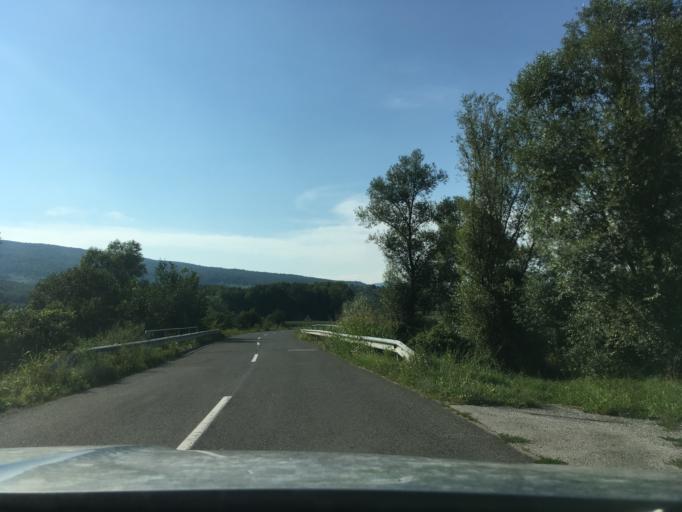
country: SI
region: Crnomelj
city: Crnomelj
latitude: 45.5228
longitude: 15.1673
